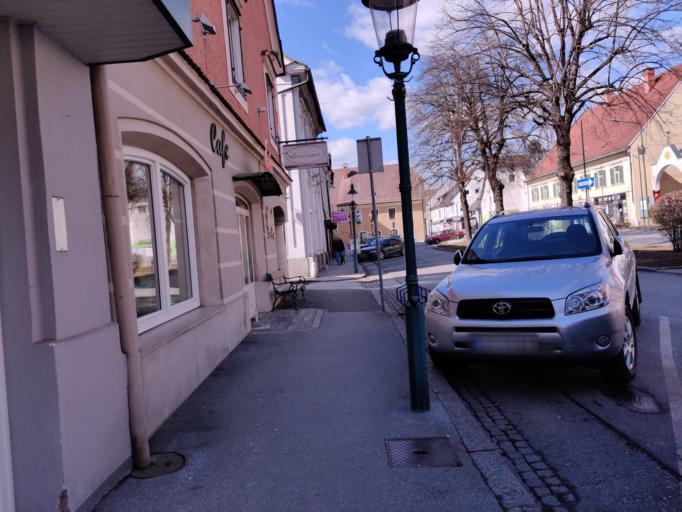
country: AT
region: Styria
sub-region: Politischer Bezirk Voitsberg
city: Voitsberg
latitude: 47.0498
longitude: 15.1482
